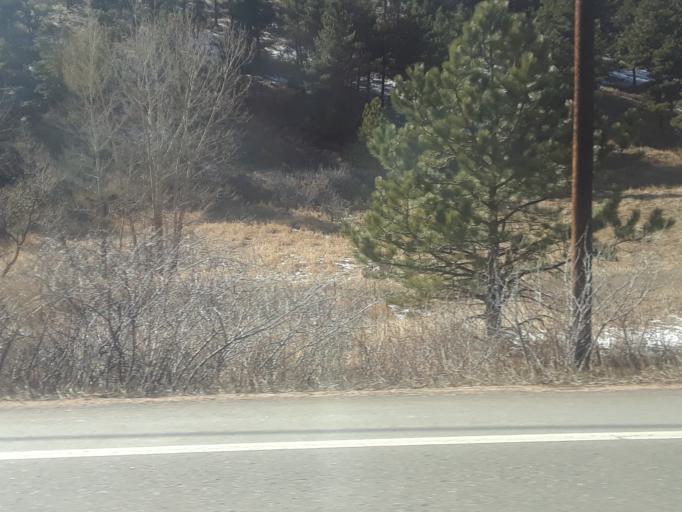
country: US
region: Colorado
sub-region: Boulder County
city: Boulder
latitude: 40.1190
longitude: -105.3069
